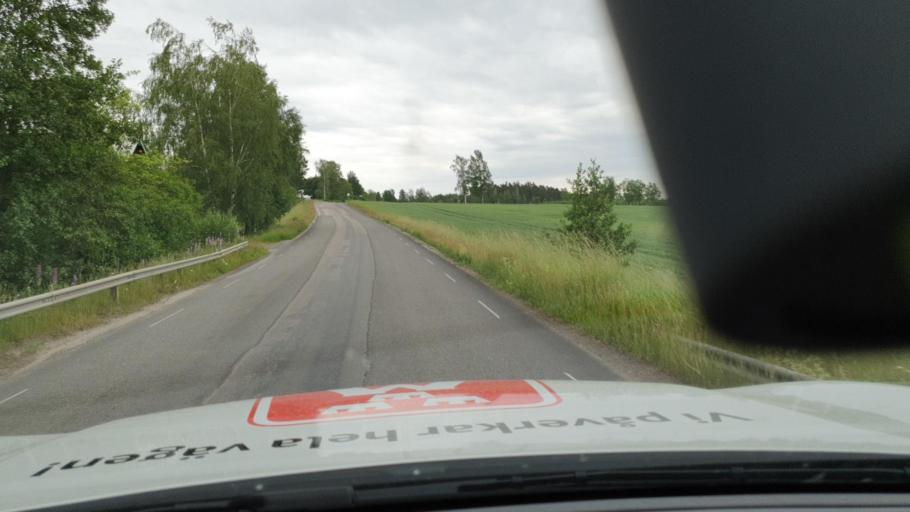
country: SE
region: Vaestra Goetaland
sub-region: Skovde Kommun
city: Skoevde
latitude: 58.3713
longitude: 13.9349
